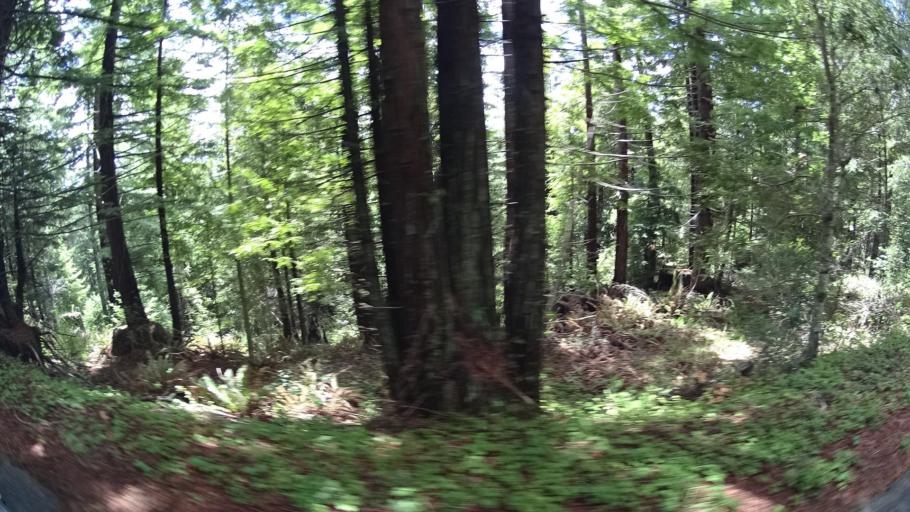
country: US
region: California
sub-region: Humboldt County
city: Blue Lake
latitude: 40.8448
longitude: -123.9239
